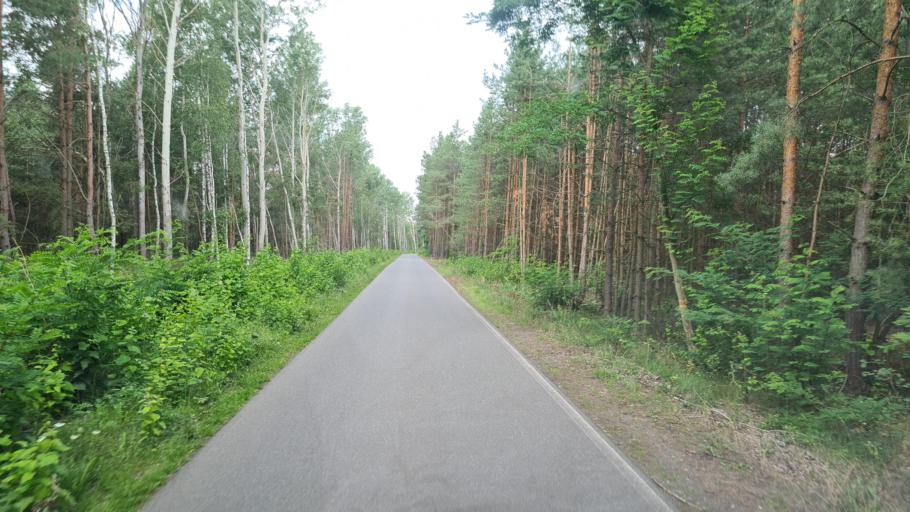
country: DE
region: Brandenburg
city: Neupetershain
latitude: 51.6822
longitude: 14.1165
